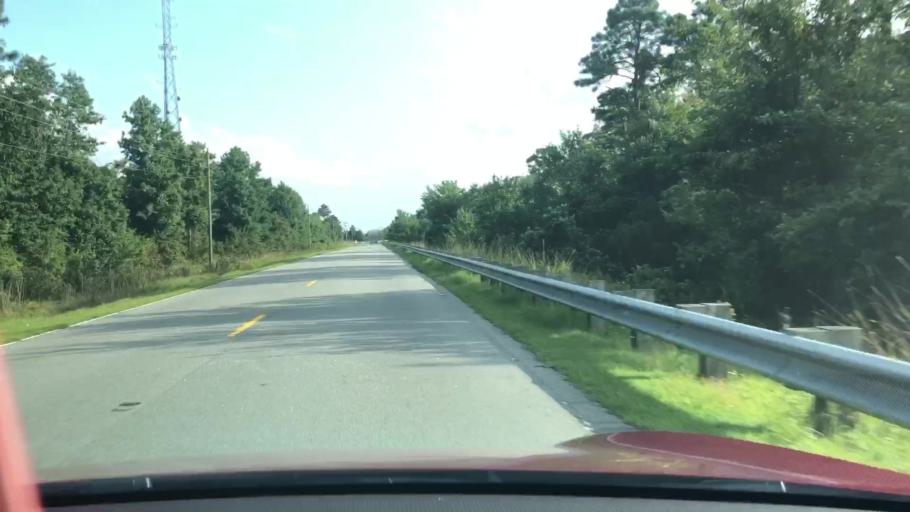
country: US
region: North Carolina
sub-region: Dare County
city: Wanchese
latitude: 35.7117
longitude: -75.7684
